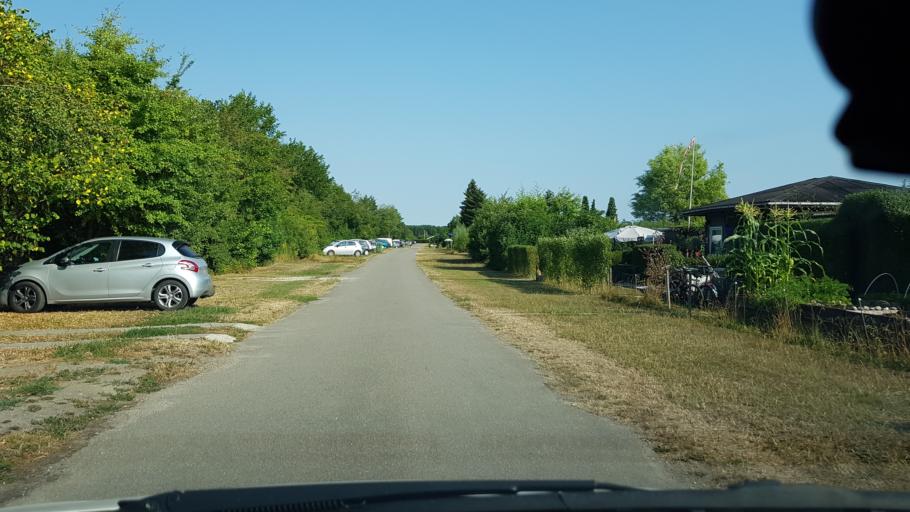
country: DK
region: Capital Region
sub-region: Vallensbaek Kommune
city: Vallensbaek
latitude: 55.6324
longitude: 12.3900
